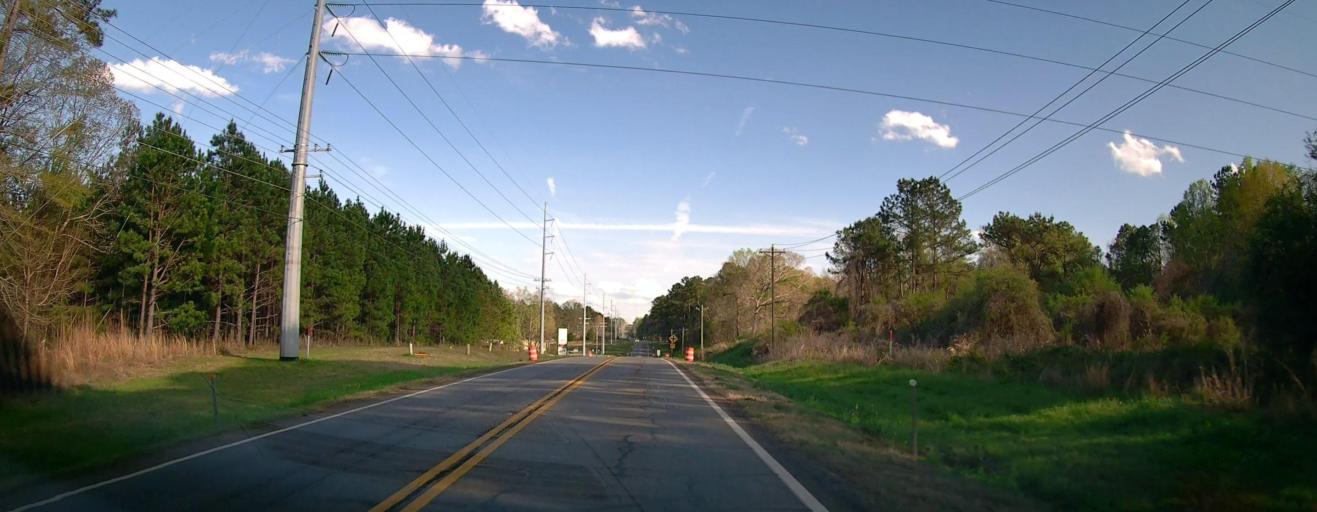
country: US
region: Georgia
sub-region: Baldwin County
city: Milledgeville
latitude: 33.1558
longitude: -83.3496
